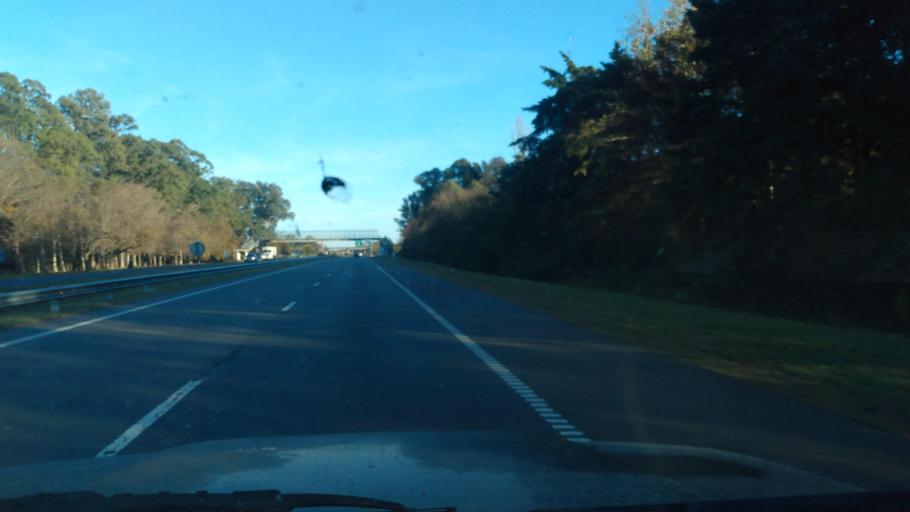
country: AR
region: Buenos Aires
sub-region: Partido de Lujan
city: Lujan
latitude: -34.5403
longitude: -59.2486
